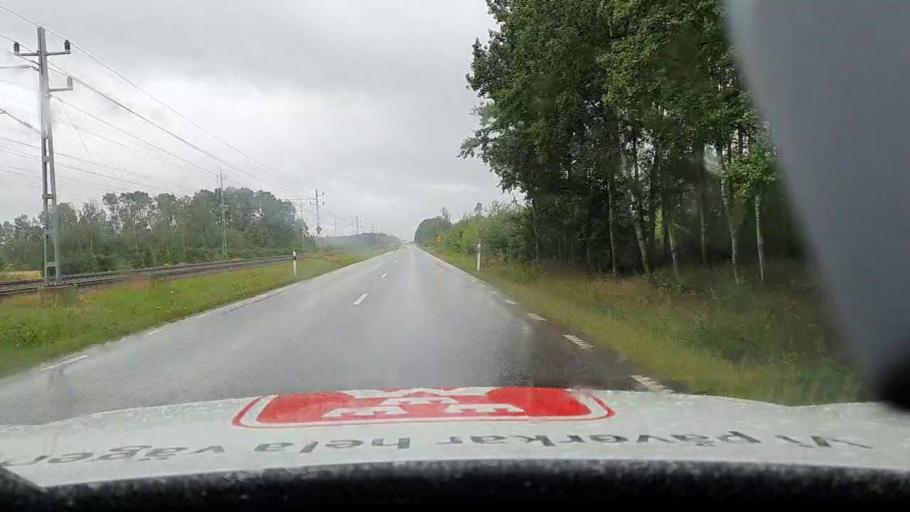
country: SE
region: Vaestra Goetaland
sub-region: Toreboda Kommun
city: Toereboda
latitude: 58.6828
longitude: 14.1072
